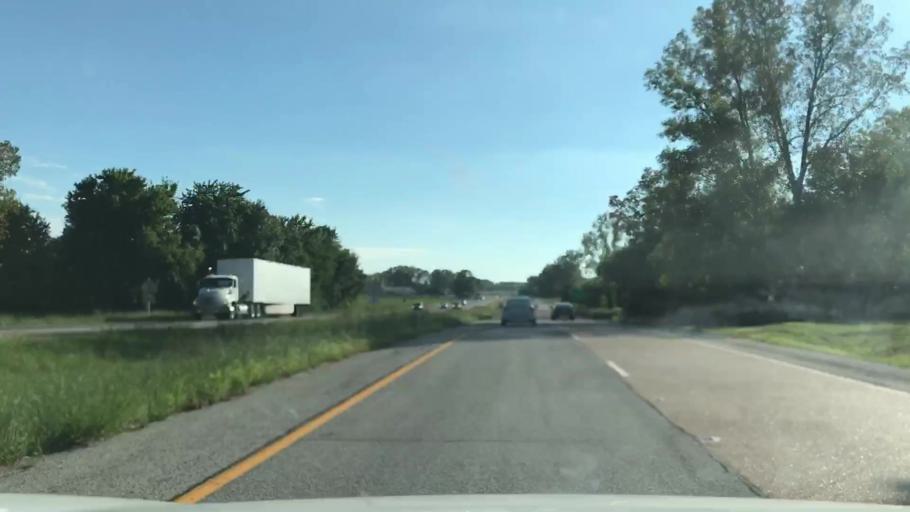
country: US
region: Illinois
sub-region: Madison County
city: Mitchell
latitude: 38.7764
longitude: -90.1149
